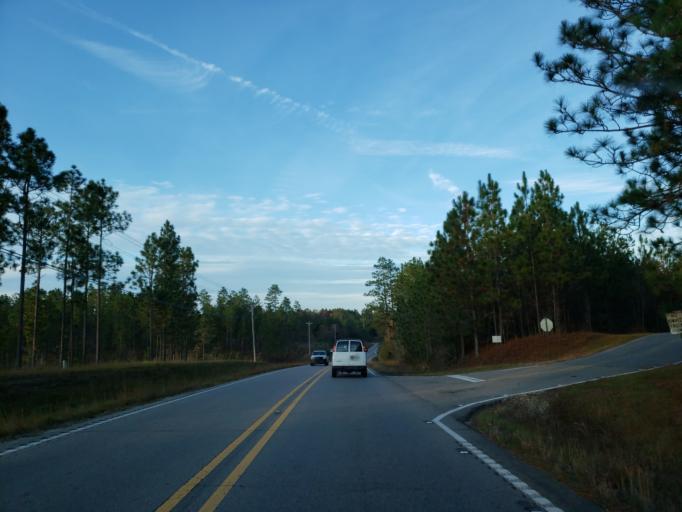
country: US
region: Mississippi
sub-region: Lamar County
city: West Hattiesburg
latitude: 31.2398
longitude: -89.3481
